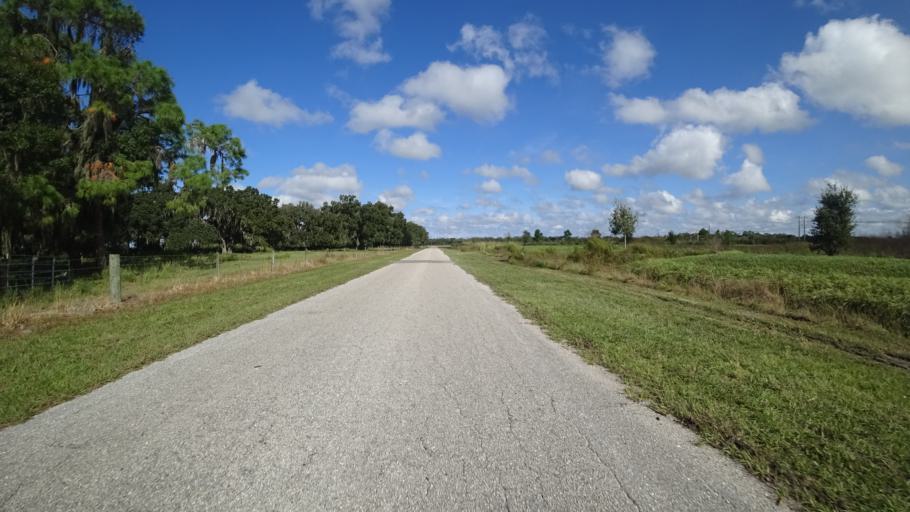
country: US
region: Florida
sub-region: Manatee County
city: Ellenton
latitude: 27.5832
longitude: -82.4614
